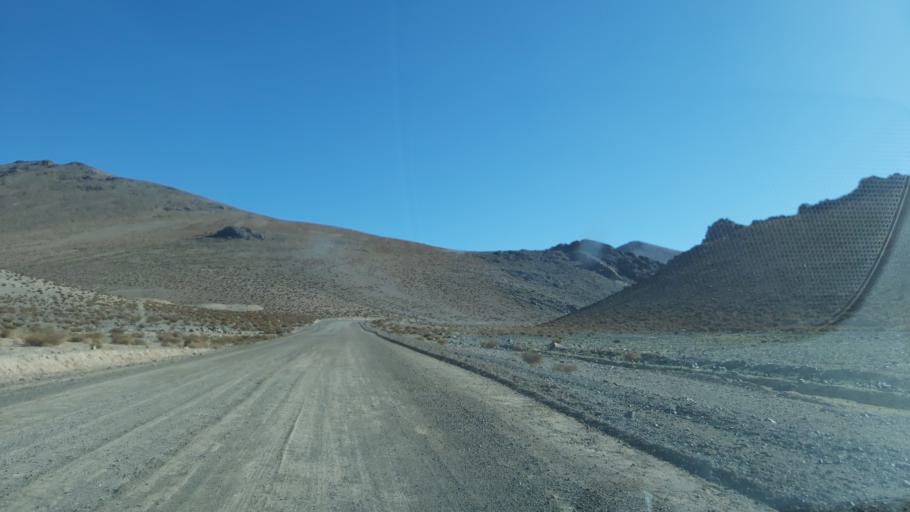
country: CL
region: Atacama
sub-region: Provincia de Chanaral
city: Diego de Almagro
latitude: -26.3820
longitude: -69.2704
